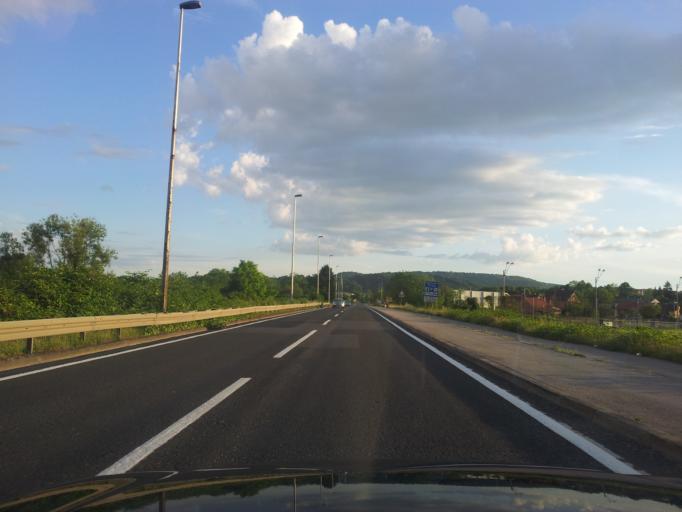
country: HR
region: Karlovacka
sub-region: Grad Karlovac
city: Karlovac
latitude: 45.4705
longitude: 15.5620
